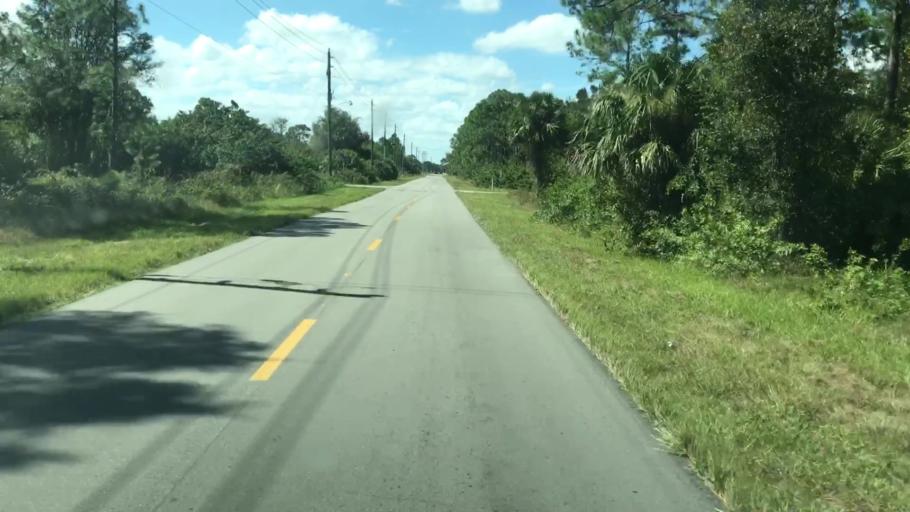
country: US
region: Florida
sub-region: Lee County
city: Lehigh Acres
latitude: 26.6612
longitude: -81.6572
